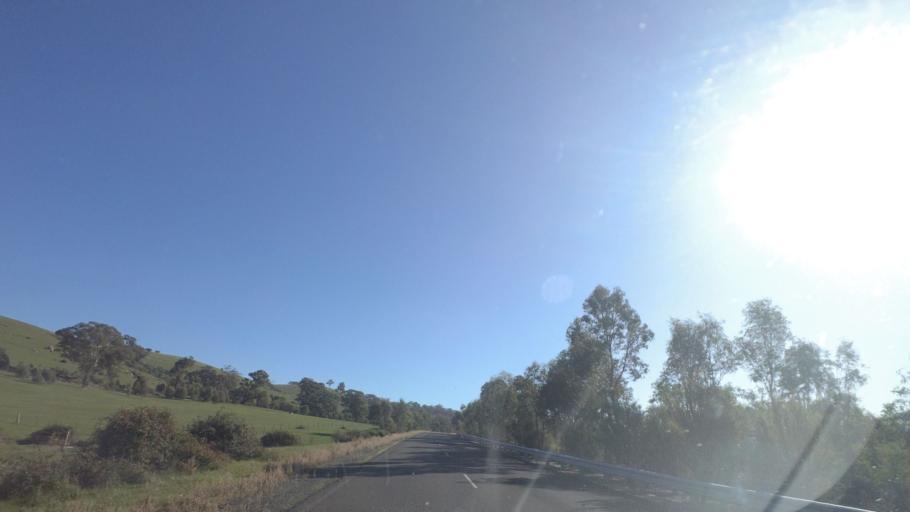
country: AU
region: Victoria
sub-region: Mount Alexander
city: Castlemaine
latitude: -37.0466
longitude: 144.2841
